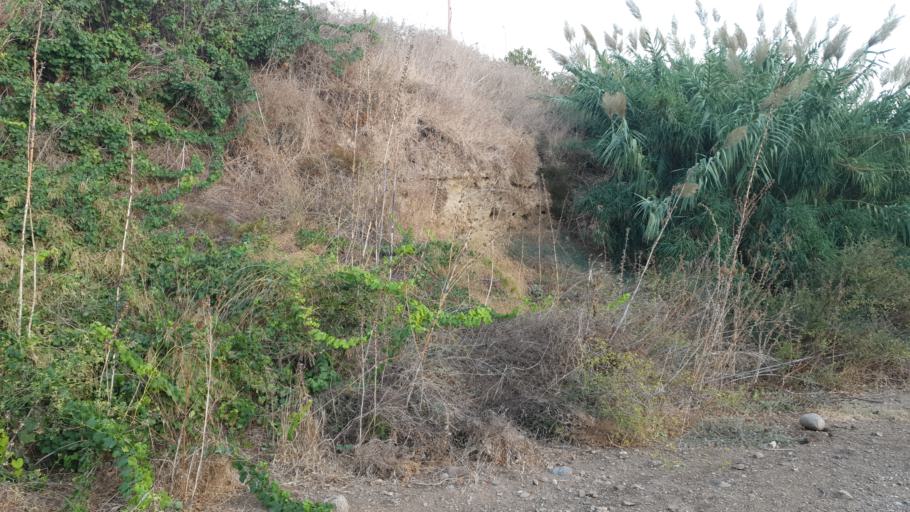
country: IL
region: Northern District
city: Qiryat Shemona
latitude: 33.2266
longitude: 35.6220
